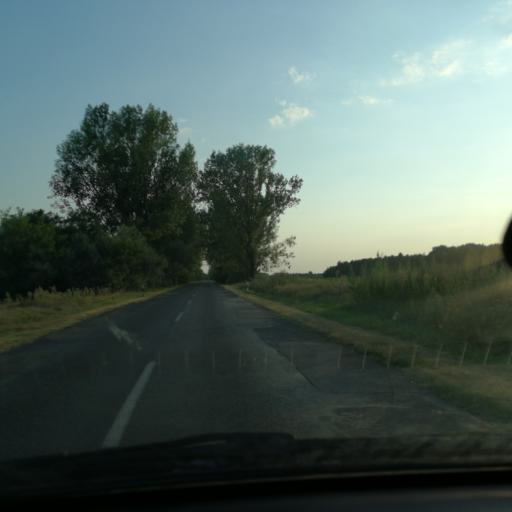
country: HU
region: Bacs-Kiskun
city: Kiskunmajsa
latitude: 46.4652
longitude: 19.6797
